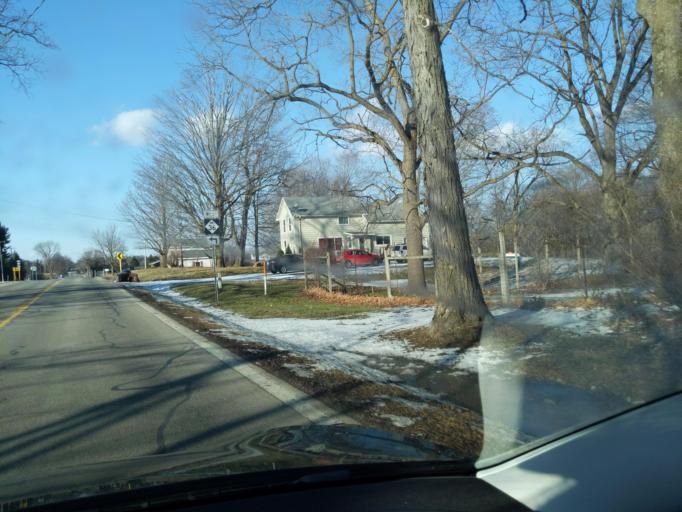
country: US
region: Michigan
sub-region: Ingham County
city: Stockbridge
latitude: 42.4811
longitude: -84.0857
